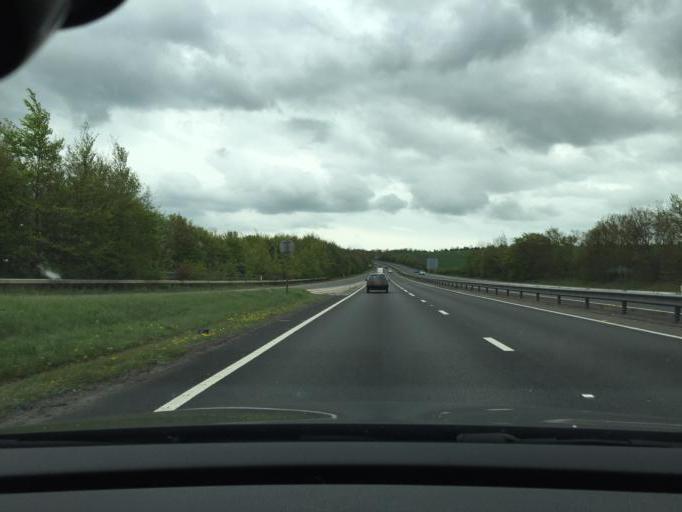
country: GB
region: England
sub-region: Oxfordshire
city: Harwell
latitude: 51.5564
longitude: -1.2995
